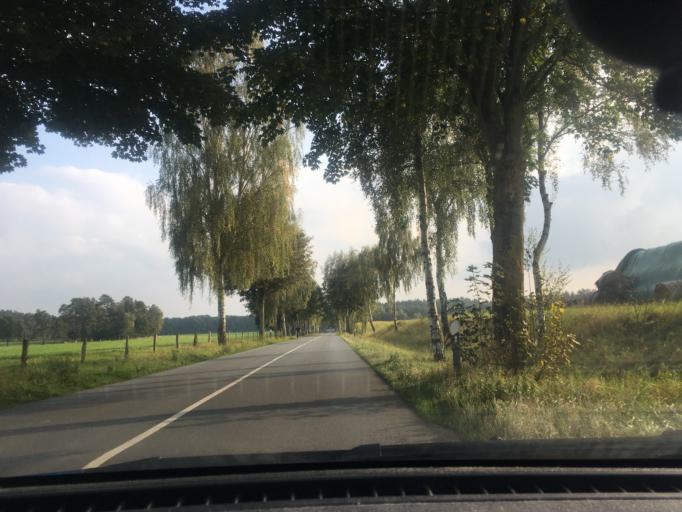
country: DE
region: Lower Saxony
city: Rullstorf
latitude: 53.2665
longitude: 10.5190
